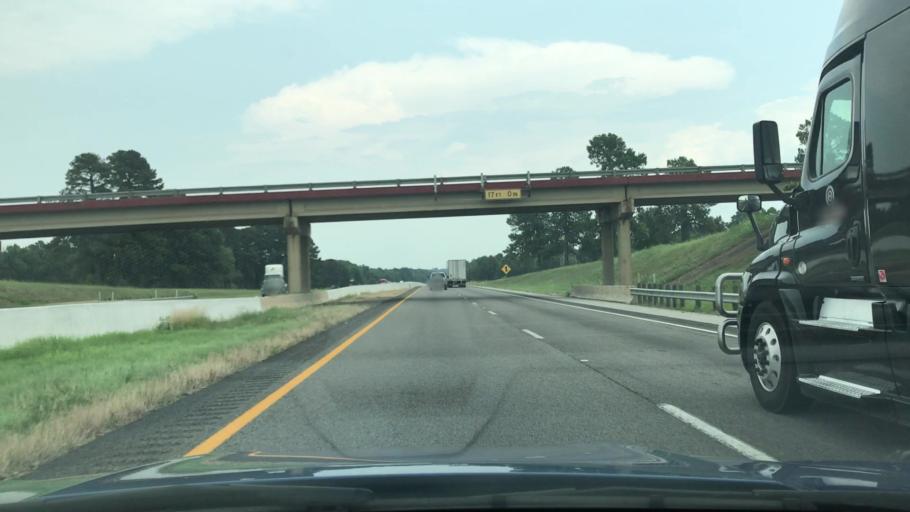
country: US
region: Texas
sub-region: Gregg County
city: Liberty City
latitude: 32.4364
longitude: -94.9902
